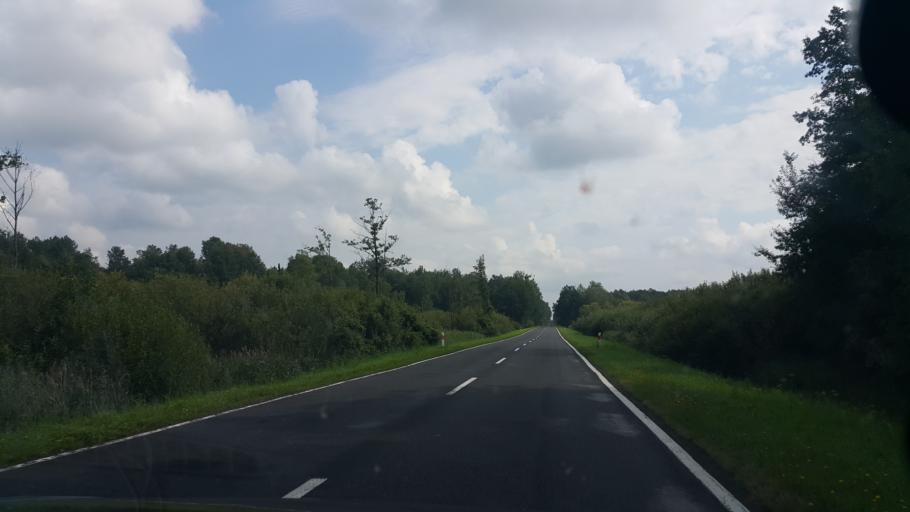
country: PL
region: Lublin Voivodeship
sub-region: Powiat wlodawski
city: Hansk
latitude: 51.4864
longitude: 23.3481
